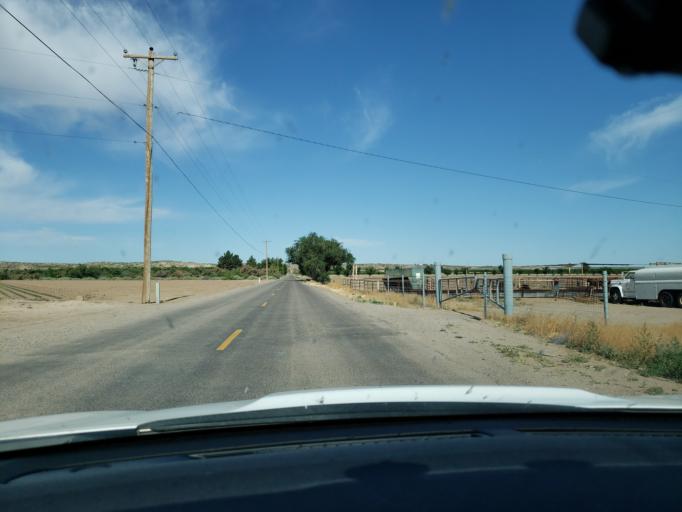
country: US
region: New Mexico
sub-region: Dona Ana County
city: Vado
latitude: 32.0826
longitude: -106.6925
